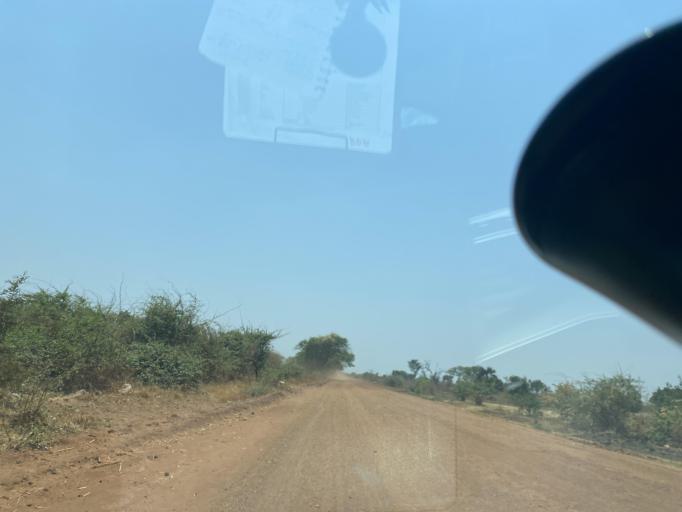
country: ZM
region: Southern
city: Nakambala
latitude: -15.4718
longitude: 27.9012
